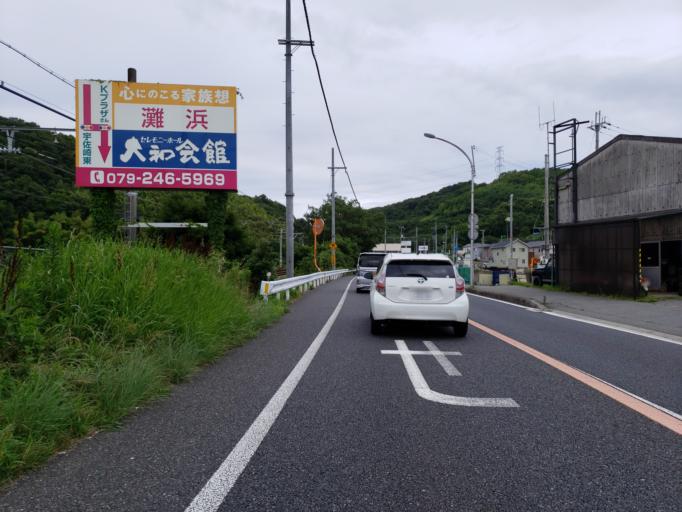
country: JP
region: Hyogo
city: Shirahamacho-usazakiminami
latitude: 34.7824
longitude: 134.7258
